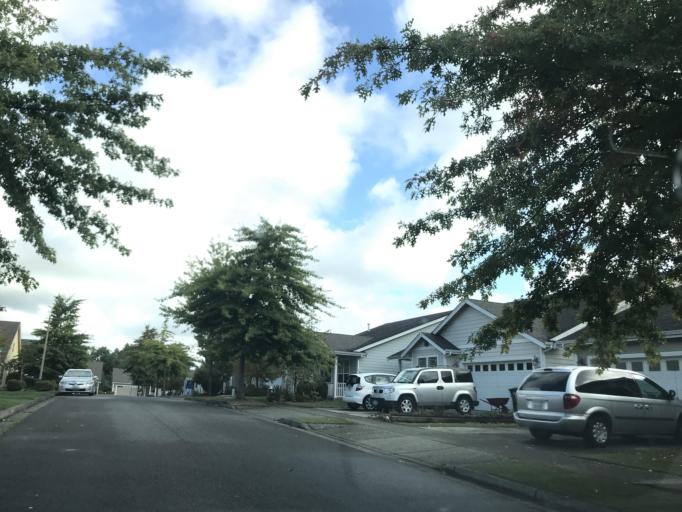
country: US
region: Washington
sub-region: Whatcom County
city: Bellingham
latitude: 48.7919
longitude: -122.5009
